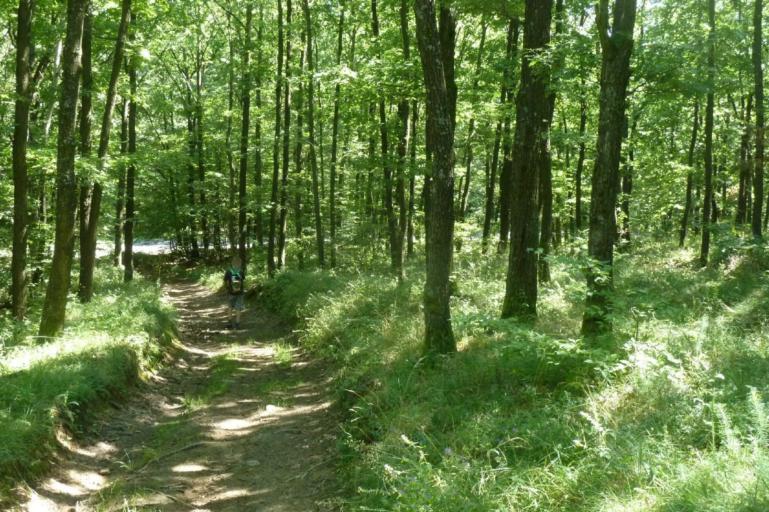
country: HU
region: Pest
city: Szob
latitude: 47.8934
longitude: 18.9194
